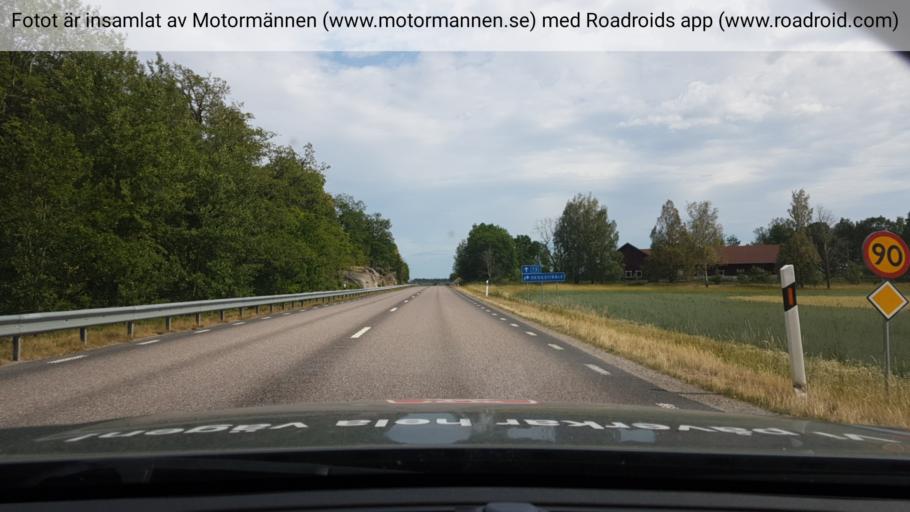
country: SE
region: Uppsala
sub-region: Enkopings Kommun
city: Orsundsbro
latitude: 59.8771
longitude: 17.2871
